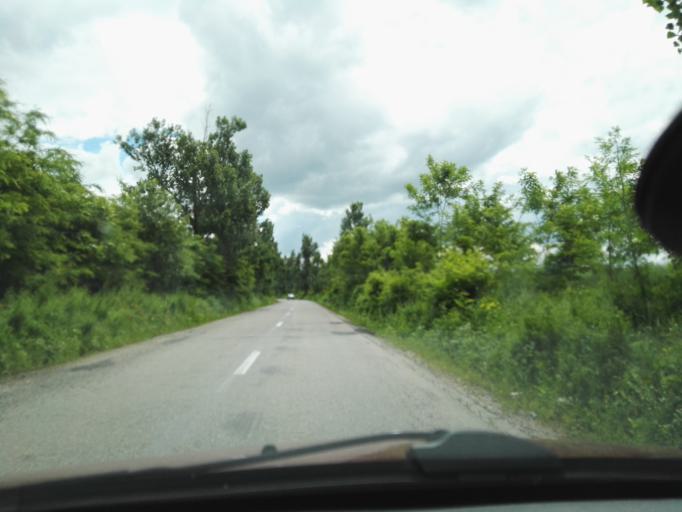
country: RO
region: Giurgiu
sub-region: Comuna Comana
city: Gradistea
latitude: 44.2327
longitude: 26.1268
